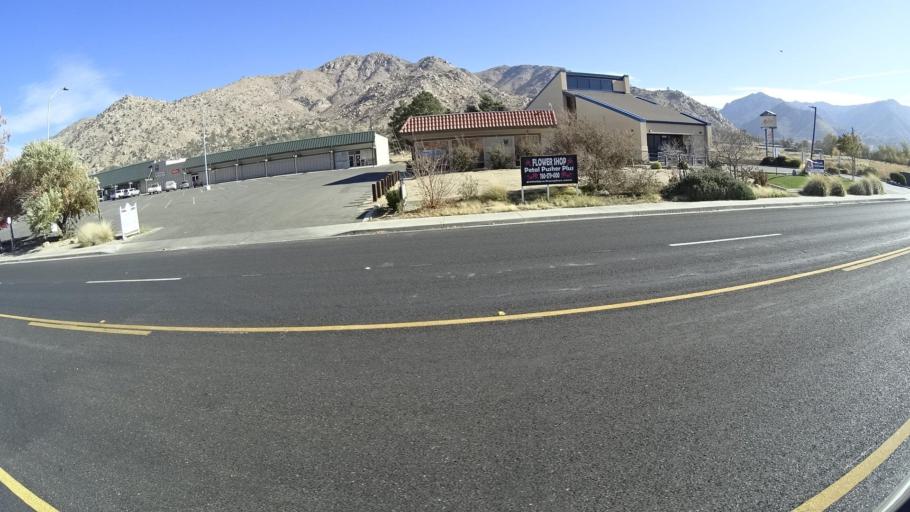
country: US
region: California
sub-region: Kern County
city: Lake Isabella
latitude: 35.6229
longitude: -118.4763
